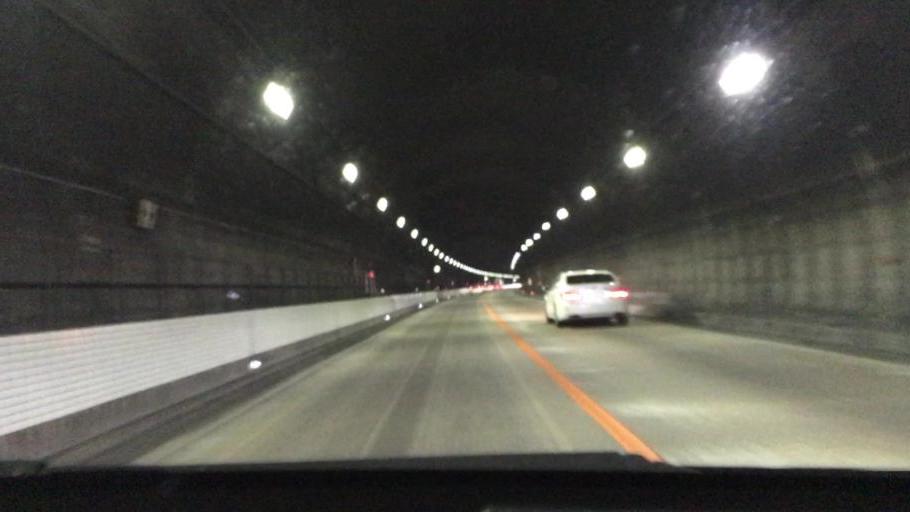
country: JP
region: Yamaguchi
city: Tokuyama
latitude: 34.0845
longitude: 131.7434
